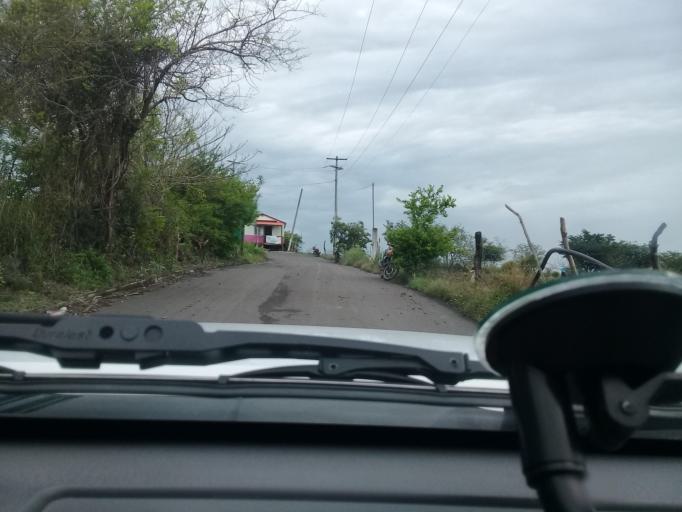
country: MX
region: Veracruz
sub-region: Puente Nacional
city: Cabezas
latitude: 19.3336
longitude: -96.3860
